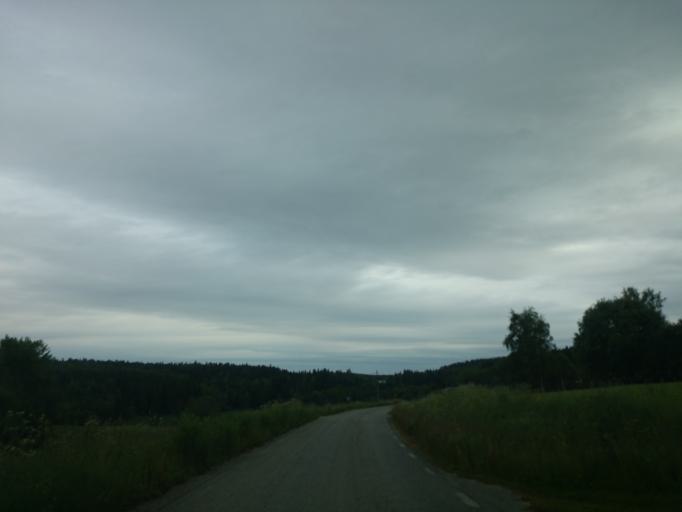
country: SE
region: Vaesternorrland
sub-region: Haernoesands Kommun
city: Haernoesand
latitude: 62.5375
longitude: 17.8210
